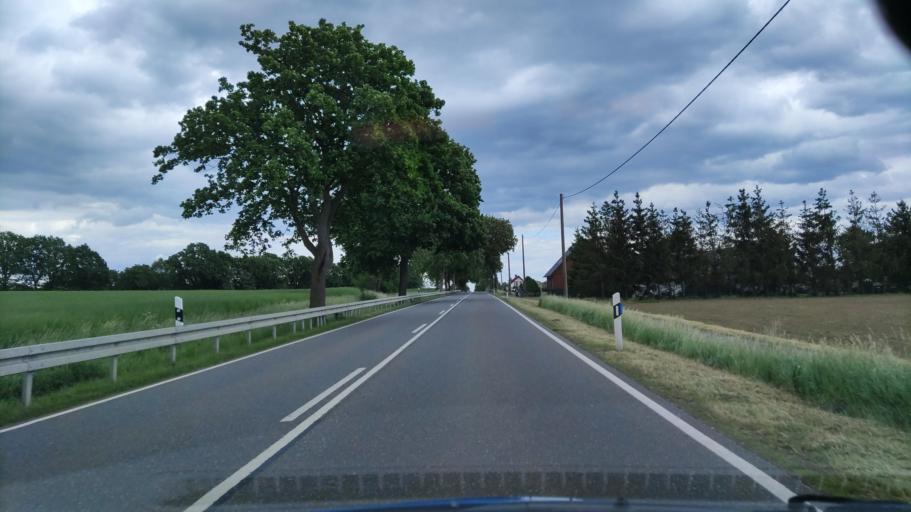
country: DE
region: Mecklenburg-Vorpommern
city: Lubz
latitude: 53.4660
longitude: 12.1014
